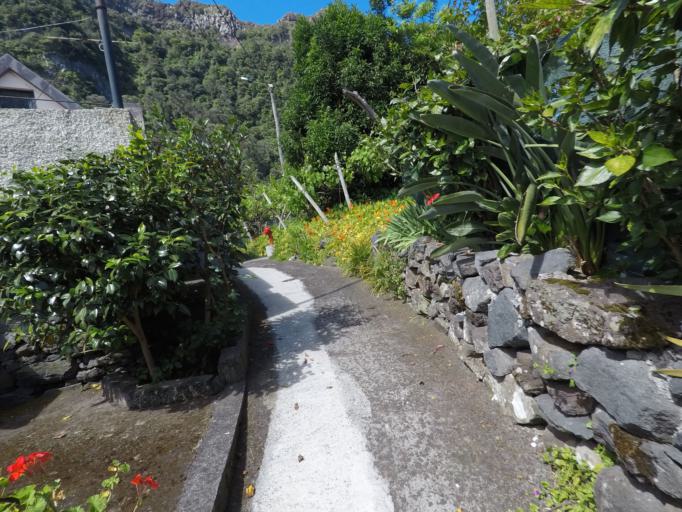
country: PT
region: Madeira
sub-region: Santana
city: Santana
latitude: 32.8252
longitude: -16.9597
